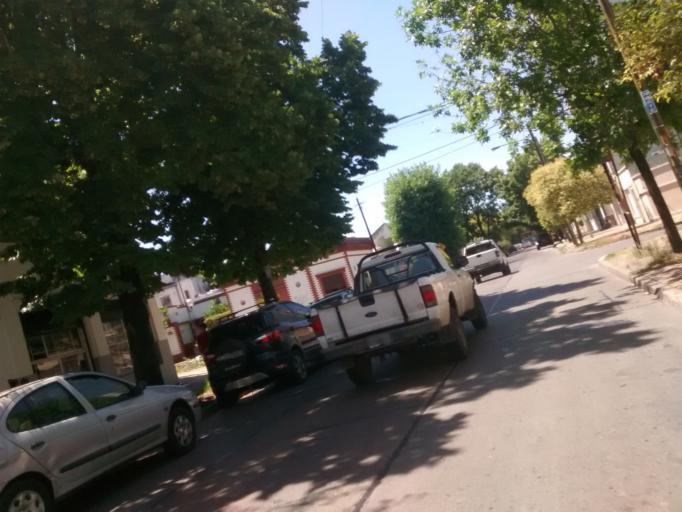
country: AR
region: Buenos Aires
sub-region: Partido de La Plata
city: La Plata
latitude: -34.8999
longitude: -57.9585
